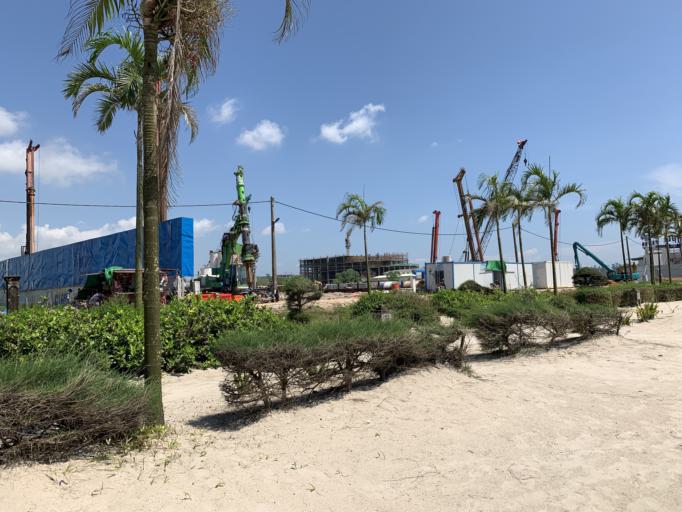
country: KH
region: Preah Sihanouk
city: Sihanoukville
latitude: 10.5677
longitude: 103.5541
